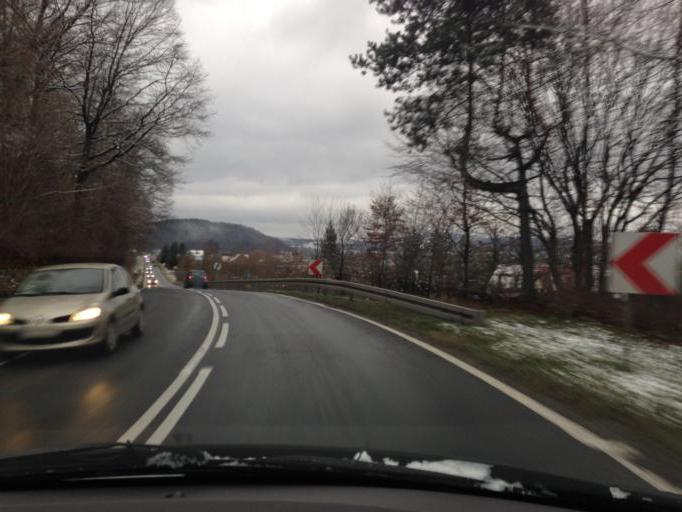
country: PL
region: Lesser Poland Voivodeship
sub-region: Powiat tarnowski
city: Zakliczyn
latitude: 49.8667
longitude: 20.7997
